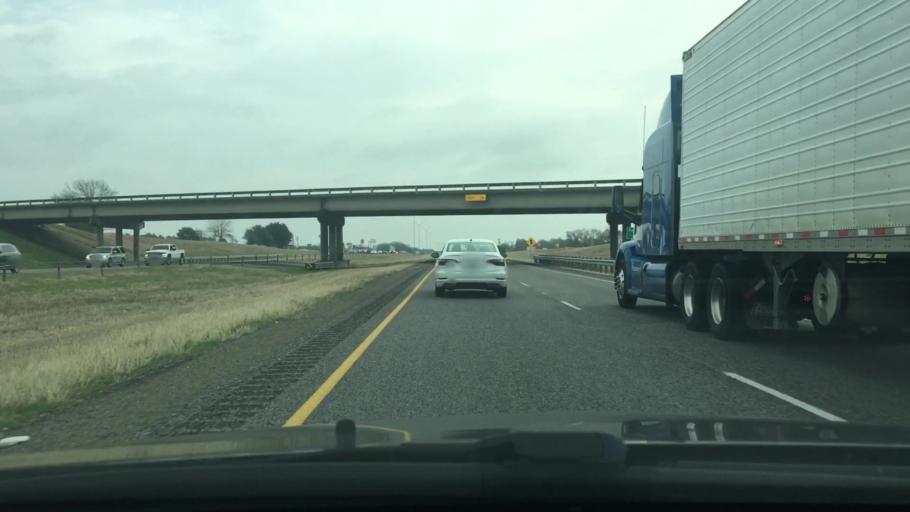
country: US
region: Texas
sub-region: Freestone County
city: Fairfield
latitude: 31.7278
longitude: -96.1807
